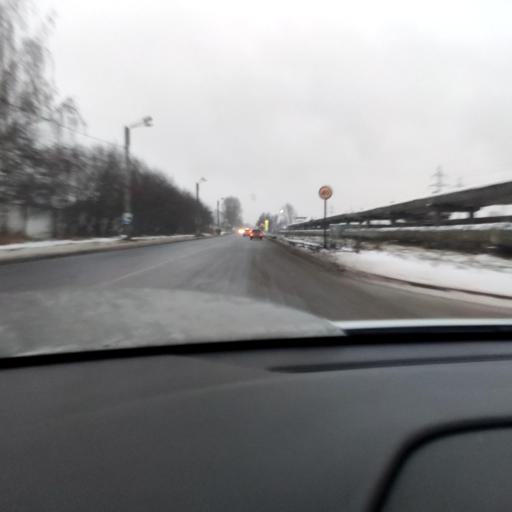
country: RU
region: Tatarstan
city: Staroye Arakchino
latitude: 55.8504
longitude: 49.0494
